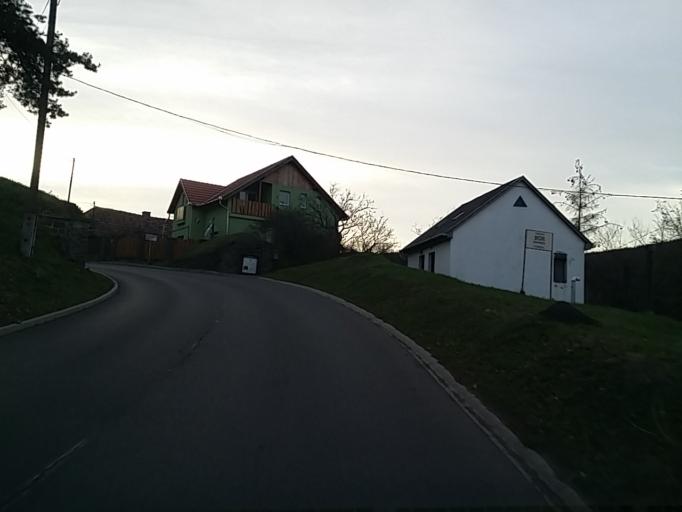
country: HU
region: Heves
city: Abasar
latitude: 47.8169
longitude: 19.9900
